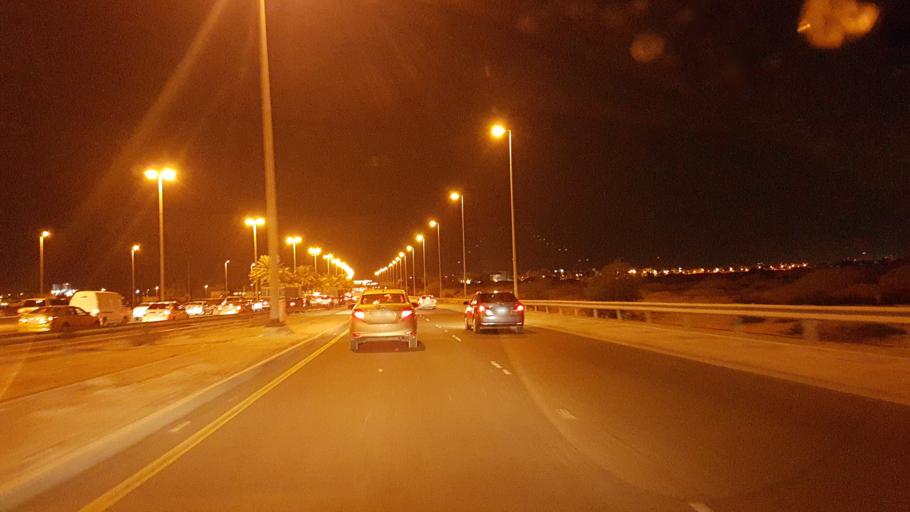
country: BH
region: Central Governorate
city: Madinat Hamad
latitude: 26.1446
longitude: 50.5103
